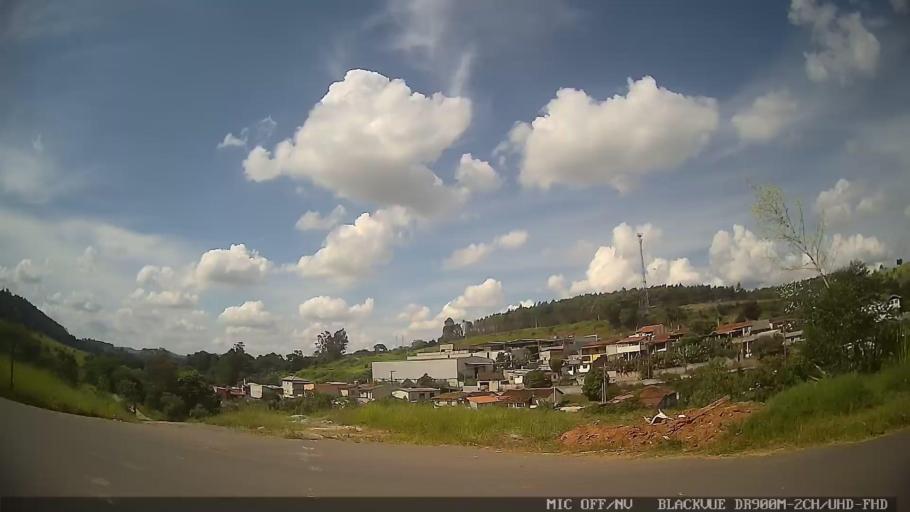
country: BR
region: Sao Paulo
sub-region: Atibaia
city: Atibaia
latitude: -23.0709
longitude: -46.5700
